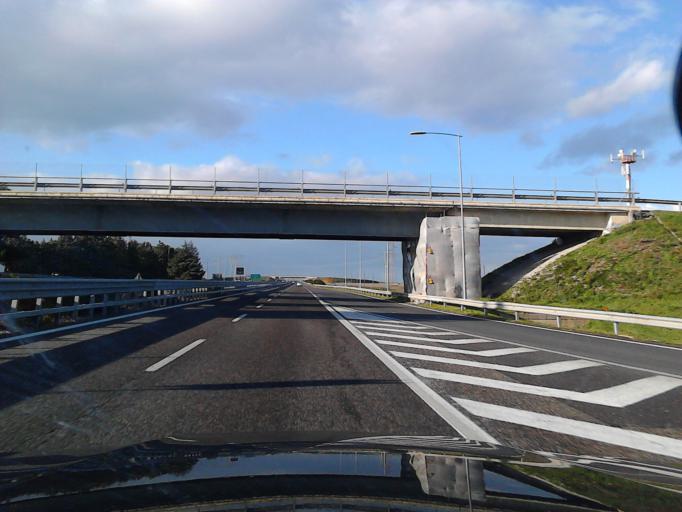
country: IT
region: Apulia
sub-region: Provincia di Foggia
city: Foggia
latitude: 41.5006
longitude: 15.5703
